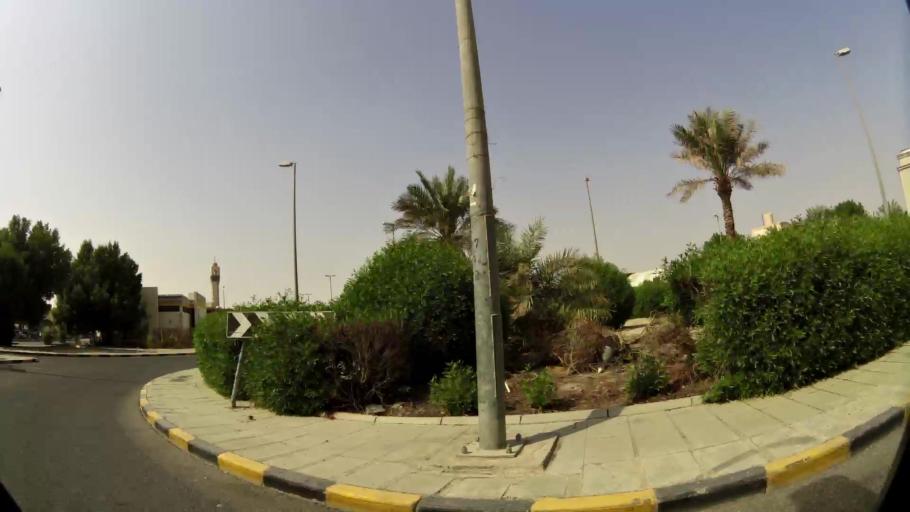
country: KW
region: Muhafazat al Jahra'
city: Al Jahra'
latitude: 29.3241
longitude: 47.6725
